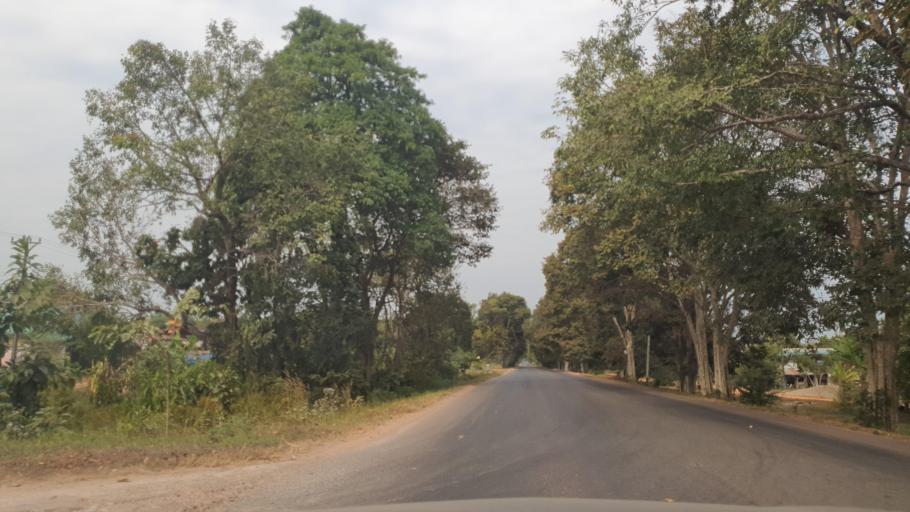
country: TH
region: Changwat Bueng Kan
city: Bung Khla
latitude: 18.2265
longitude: 104.0333
